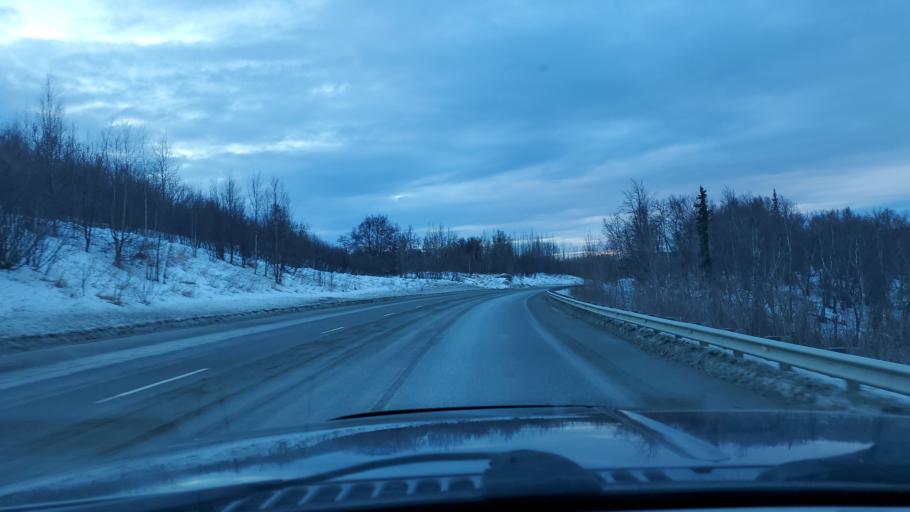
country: US
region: Alaska
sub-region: Matanuska-Susitna Borough
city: Lazy Mountain
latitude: 61.6783
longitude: -148.9945
